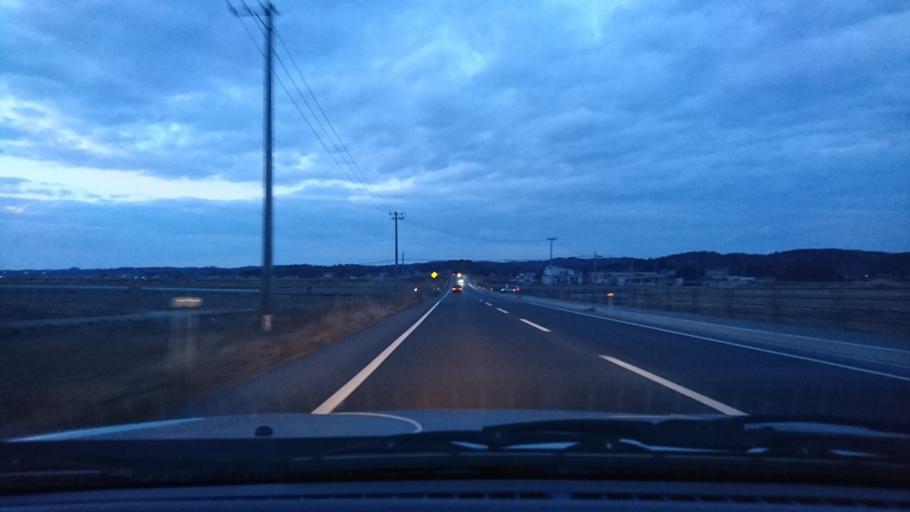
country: JP
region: Iwate
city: Ichinoseki
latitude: 38.8169
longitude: 141.1979
